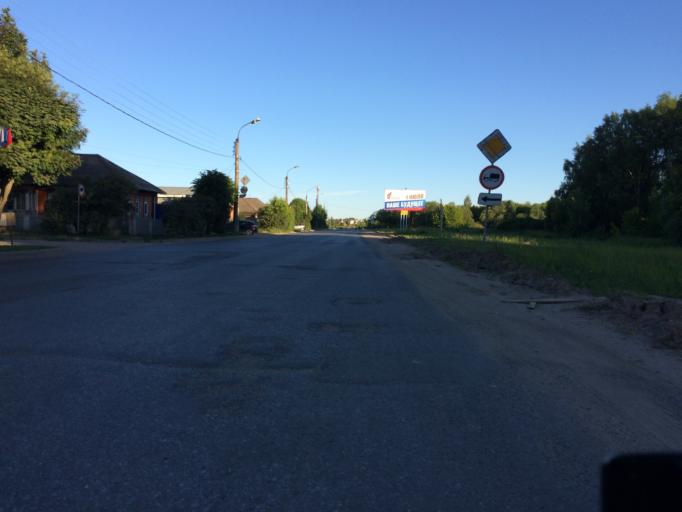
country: RU
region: Mariy-El
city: Medvedevo
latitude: 56.6525
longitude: 47.8460
